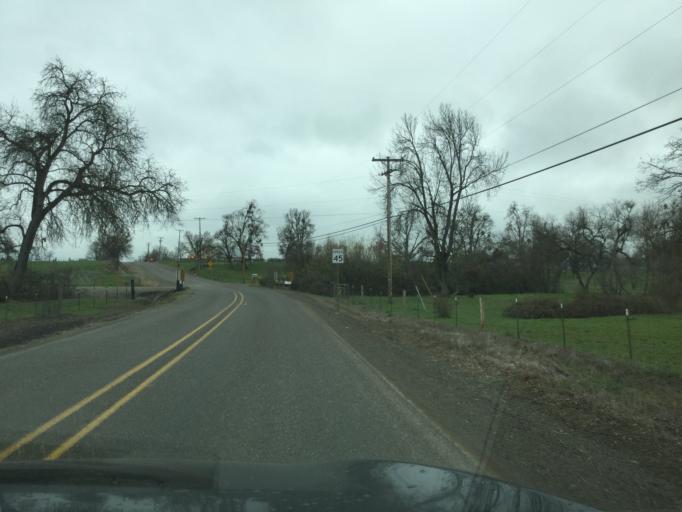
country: US
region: Oregon
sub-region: Jackson County
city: Central Point
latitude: 42.4037
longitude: -122.9092
